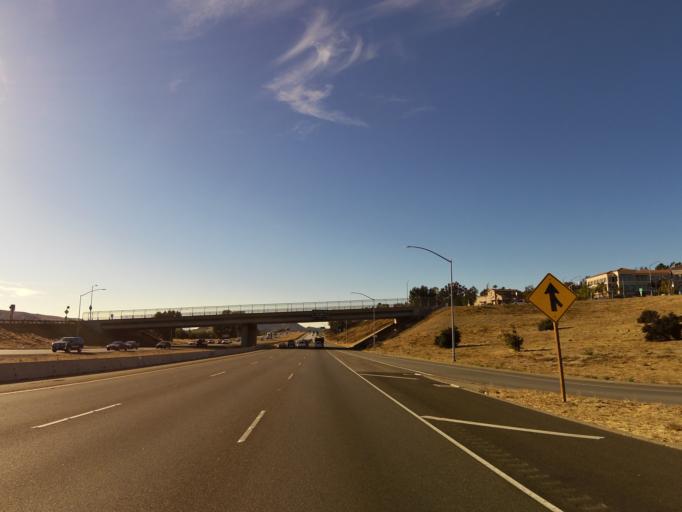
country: US
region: California
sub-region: Ventura County
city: Simi Valley
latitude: 34.2825
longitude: -118.7773
